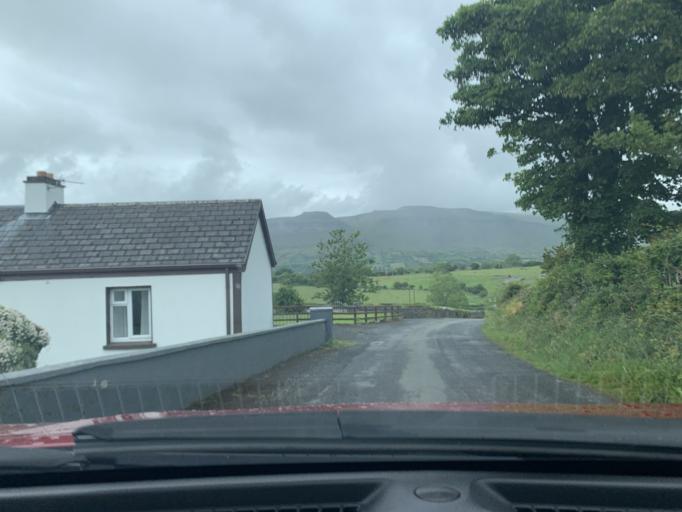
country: IE
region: Connaught
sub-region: Sligo
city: Sligo
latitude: 54.3089
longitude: -8.4552
